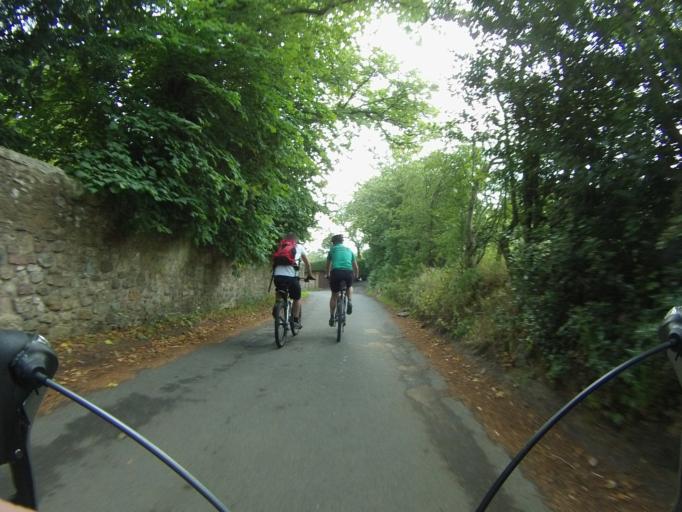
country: GB
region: Scotland
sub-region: Edinburgh
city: Colinton
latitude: 55.8971
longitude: -3.2606
